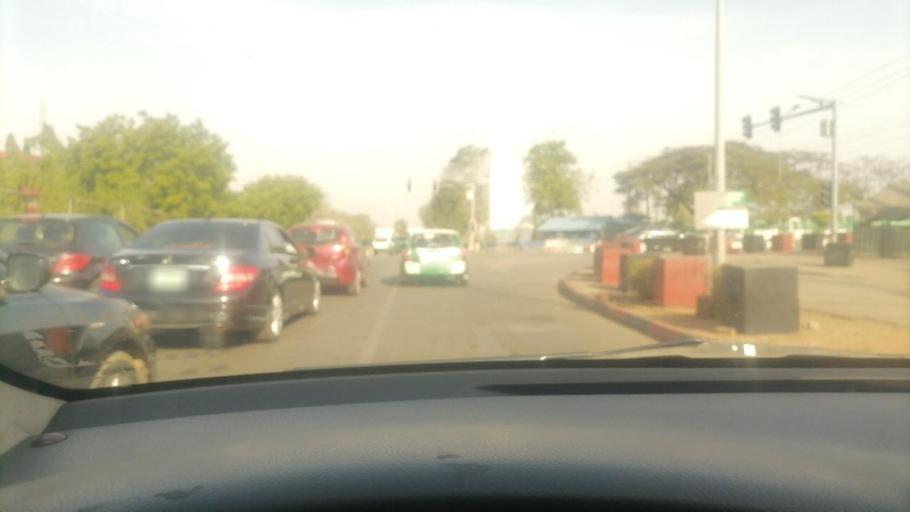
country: NG
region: Abuja Federal Capital Territory
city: Abuja
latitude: 9.0403
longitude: 7.4881
